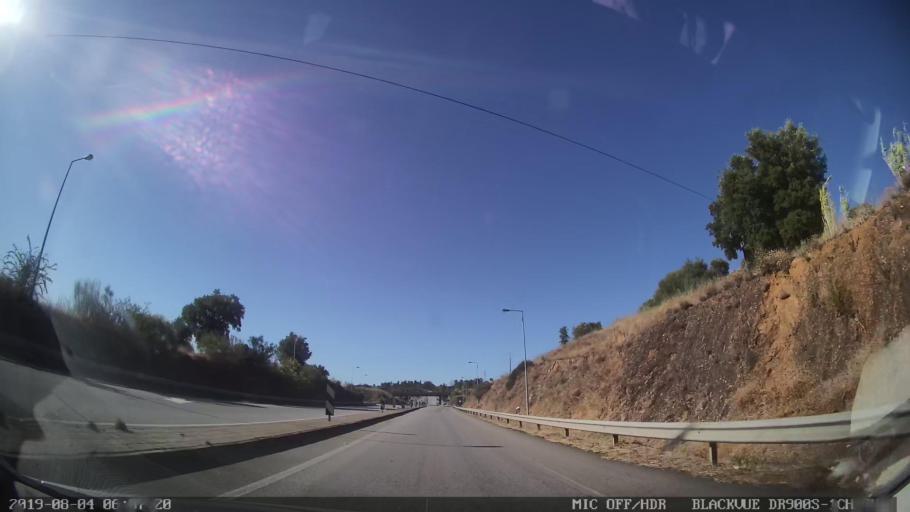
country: PT
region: Santarem
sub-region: Abrantes
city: Alferrarede
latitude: 39.4907
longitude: -8.0990
